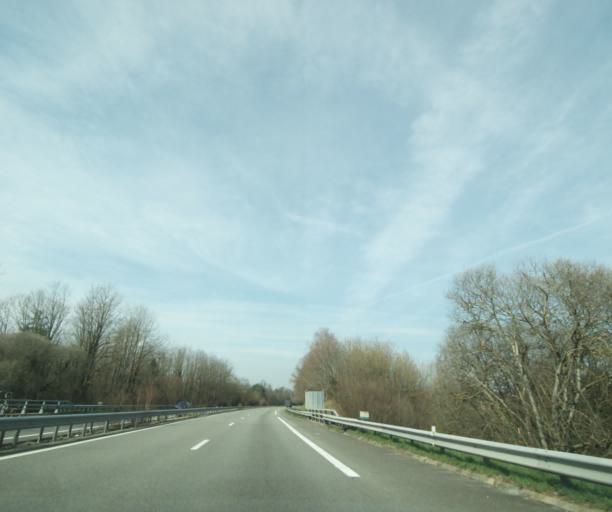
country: FR
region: Limousin
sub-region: Departement de la Haute-Vienne
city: Saint-Germain-les-Belles
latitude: 45.5922
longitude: 1.4581
